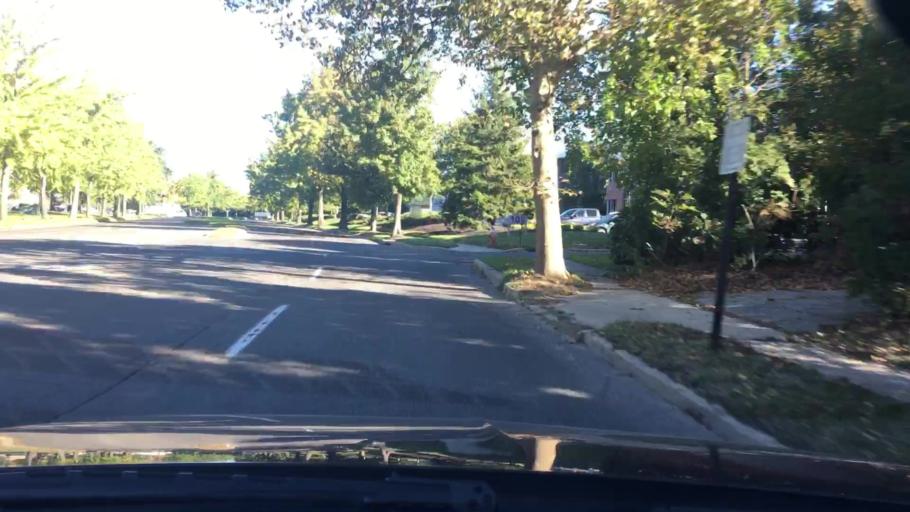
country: US
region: New York
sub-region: Suffolk County
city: Melville
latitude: 40.7714
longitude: -73.4134
